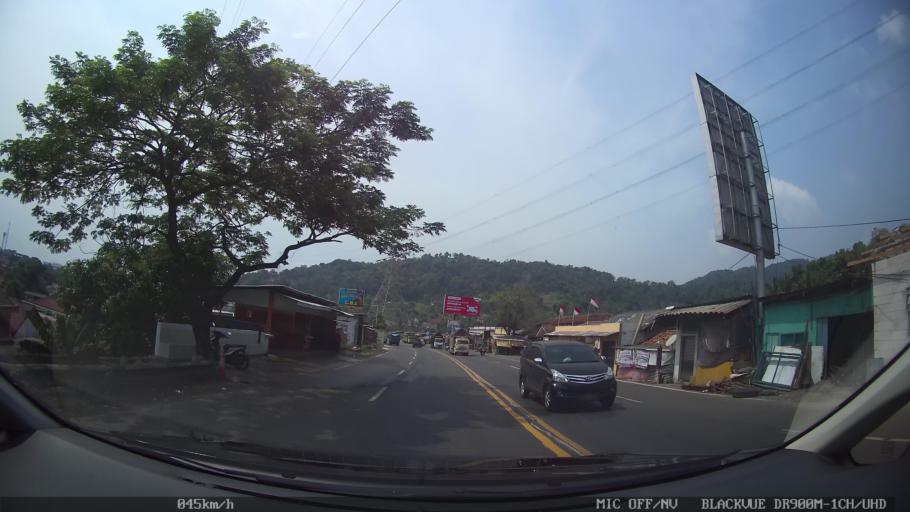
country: ID
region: Banten
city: Curug
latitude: -5.9444
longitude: 106.0047
